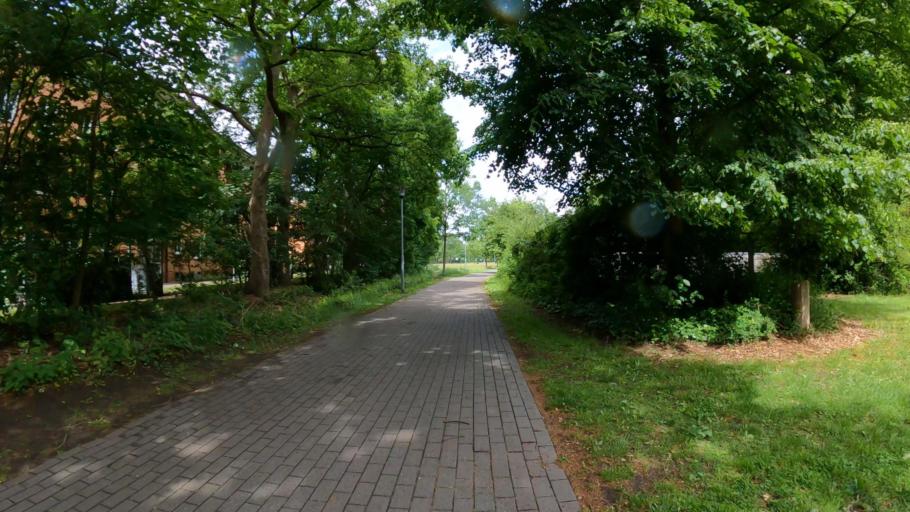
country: DE
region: Schleswig-Holstein
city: Norderstedt
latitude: 53.6901
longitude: 9.9854
